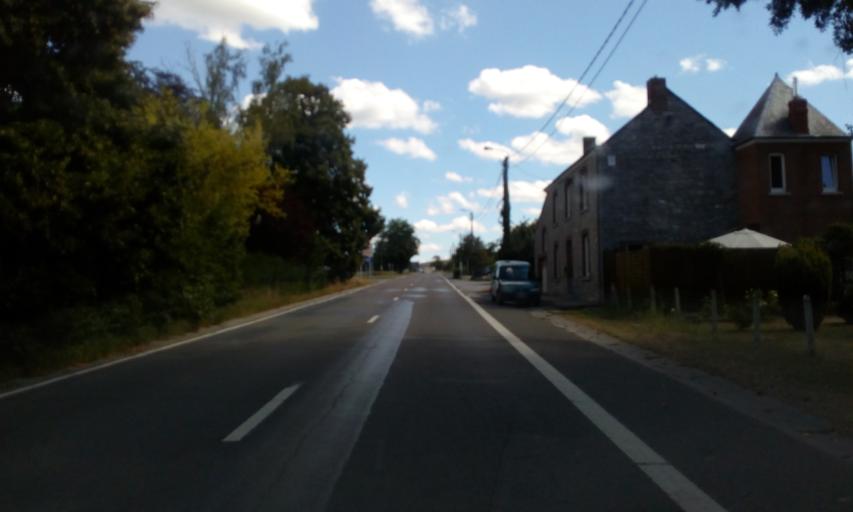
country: BE
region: Wallonia
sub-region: Province du Luxembourg
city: Wellin
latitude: 50.0804
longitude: 5.1214
